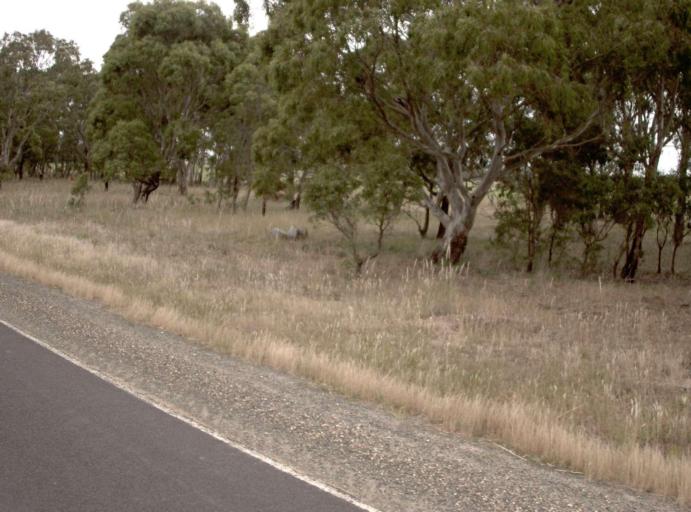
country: AU
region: Victoria
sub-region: Wellington
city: Heyfield
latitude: -38.0435
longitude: 146.7673
